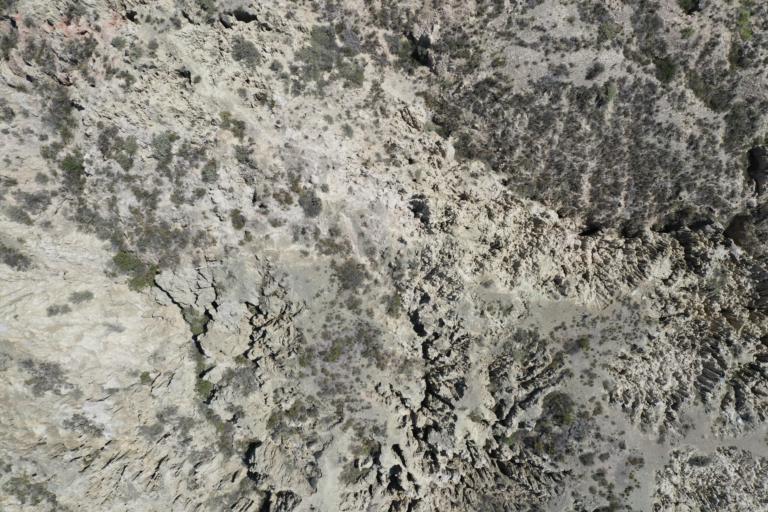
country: BO
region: La Paz
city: La Paz
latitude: -16.5613
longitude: -68.1136
